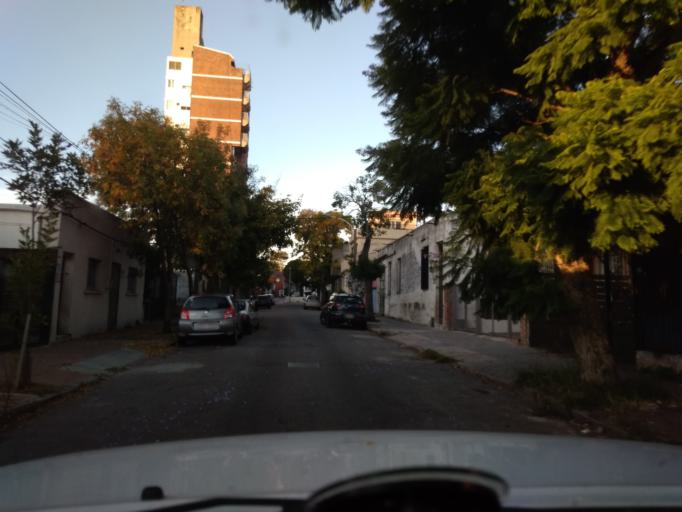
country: UY
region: Montevideo
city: Montevideo
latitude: -34.8893
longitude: -56.1441
